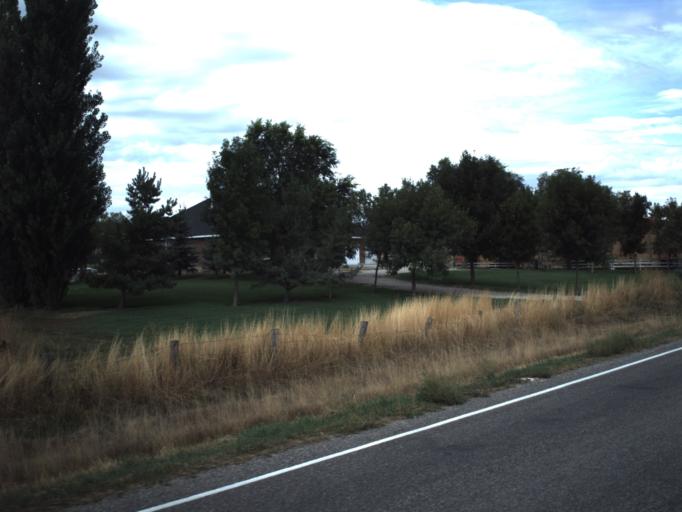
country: US
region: Utah
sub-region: Cache County
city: Lewiston
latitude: 41.9952
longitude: -111.9549
